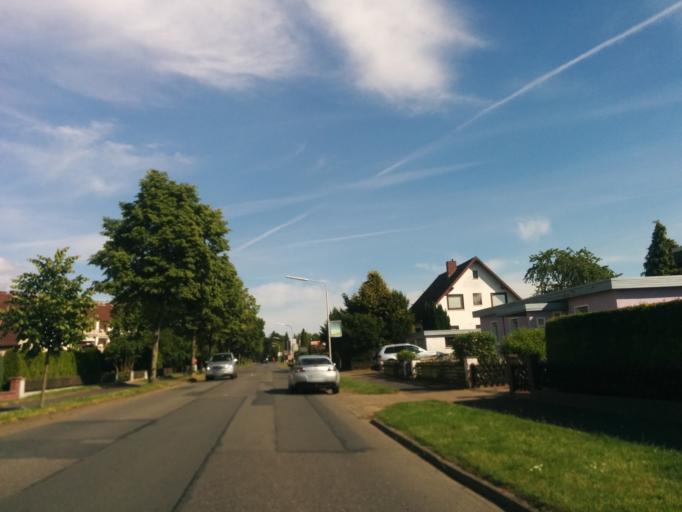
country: DE
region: Lower Saxony
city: Herzberg am Harz
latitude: 51.6619
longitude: 10.3293
